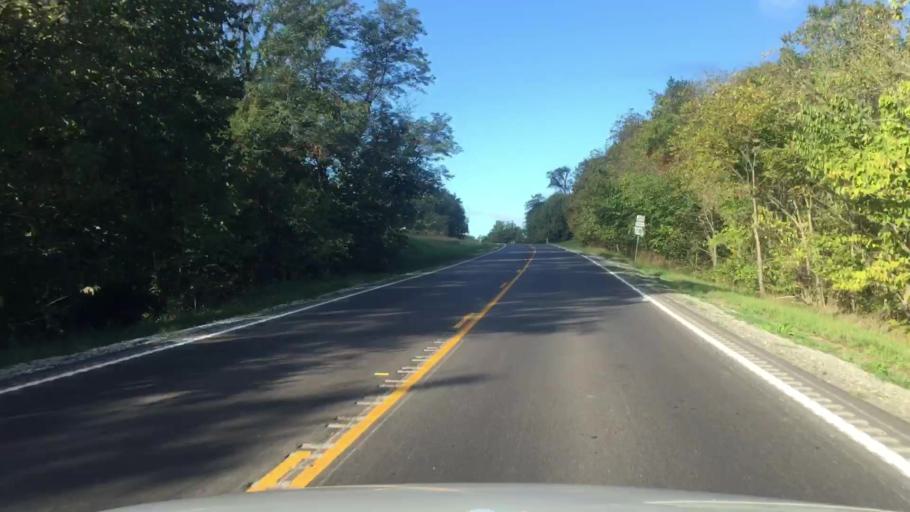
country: US
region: Missouri
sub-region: Howard County
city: New Franklin
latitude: 38.9973
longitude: -92.5977
